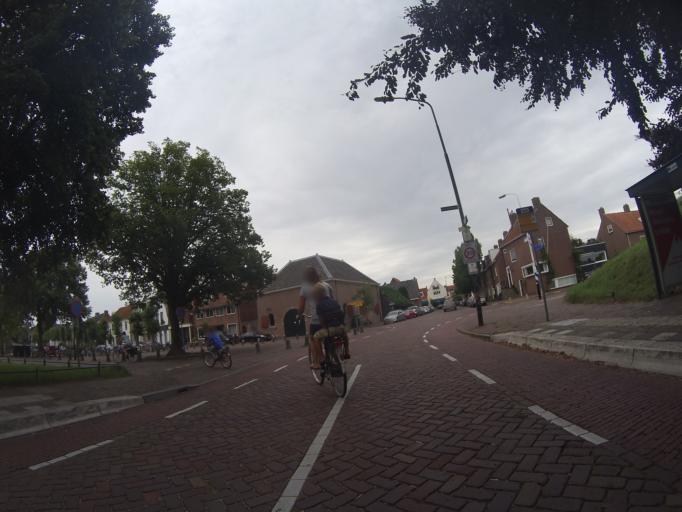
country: NL
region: North Holland
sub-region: Gemeente Naarden
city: Naarden
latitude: 52.2962
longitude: 5.1590
